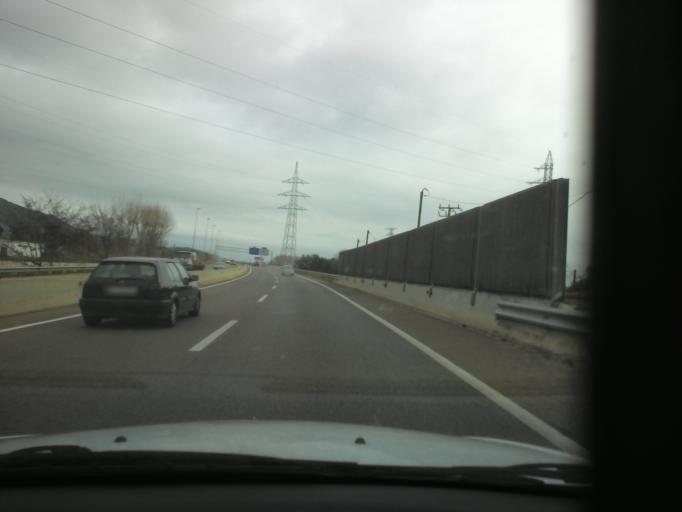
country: ES
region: Catalonia
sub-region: Provincia de Girona
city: Sant Feliu de Guixols
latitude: 41.8064
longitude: 3.0293
